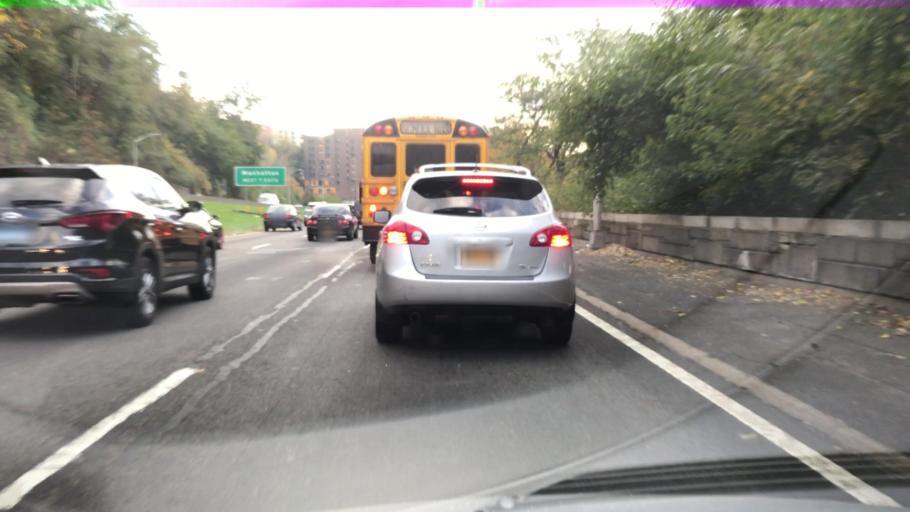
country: US
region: New York
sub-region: New York County
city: Inwood
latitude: 40.8663
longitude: -73.9094
